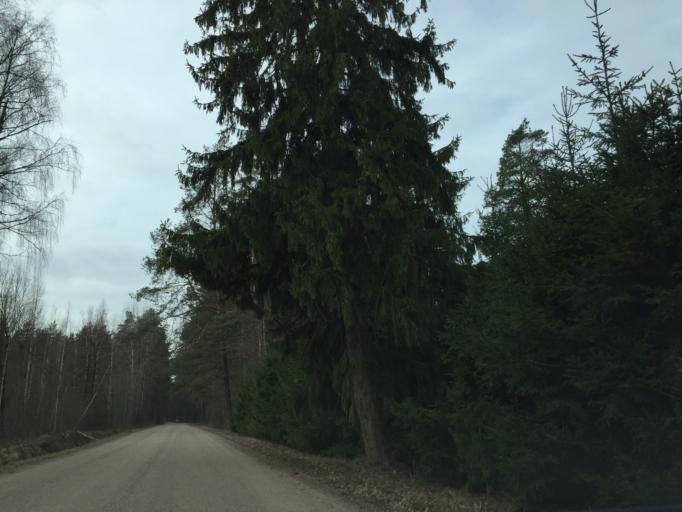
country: LV
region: Garkalne
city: Garkalne
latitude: 57.0735
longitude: 24.4372
